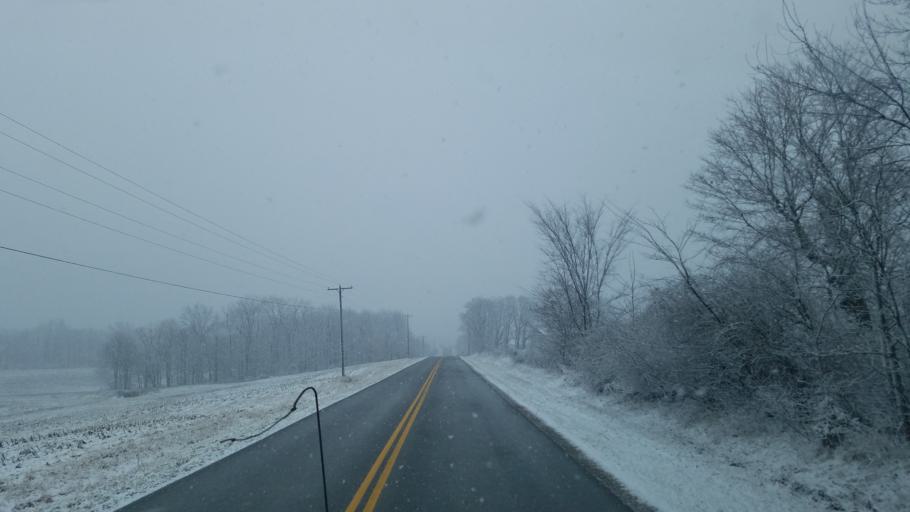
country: US
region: Ohio
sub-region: Champaign County
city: North Lewisburg
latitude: 40.3382
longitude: -83.6089
